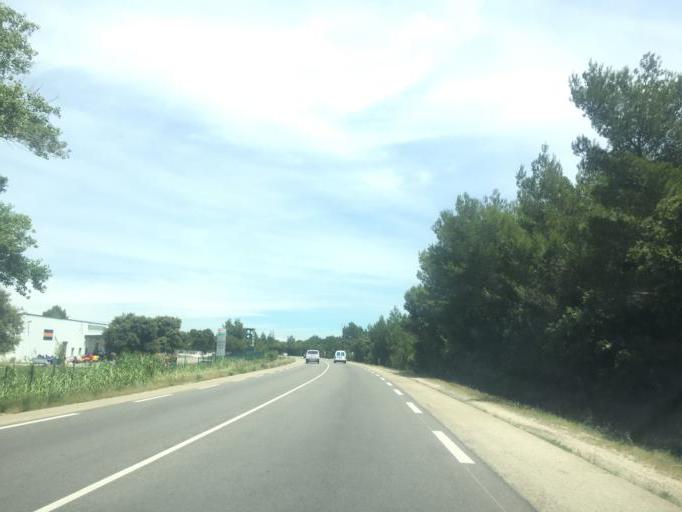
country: FR
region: Languedoc-Roussillon
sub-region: Departement du Gard
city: Les Angles
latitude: 43.9710
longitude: 4.7454
